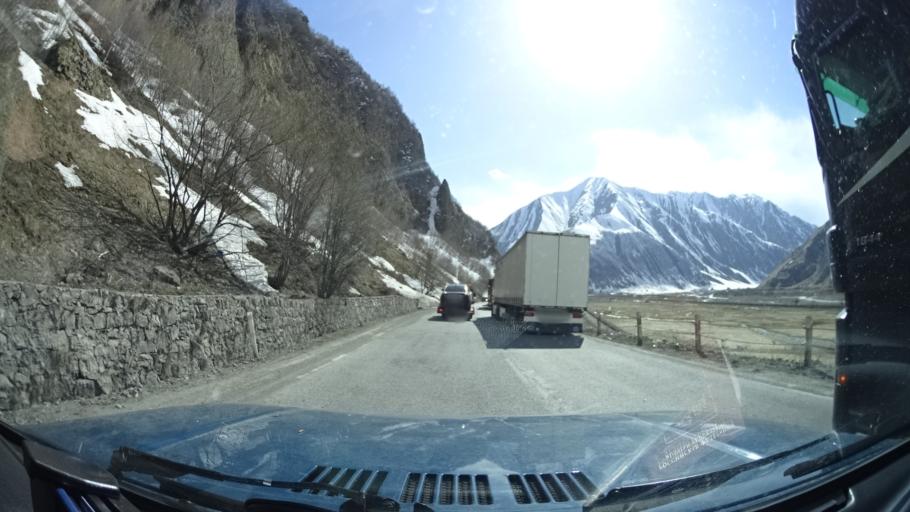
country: GE
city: Gudauri
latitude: 42.5637
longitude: 44.5176
